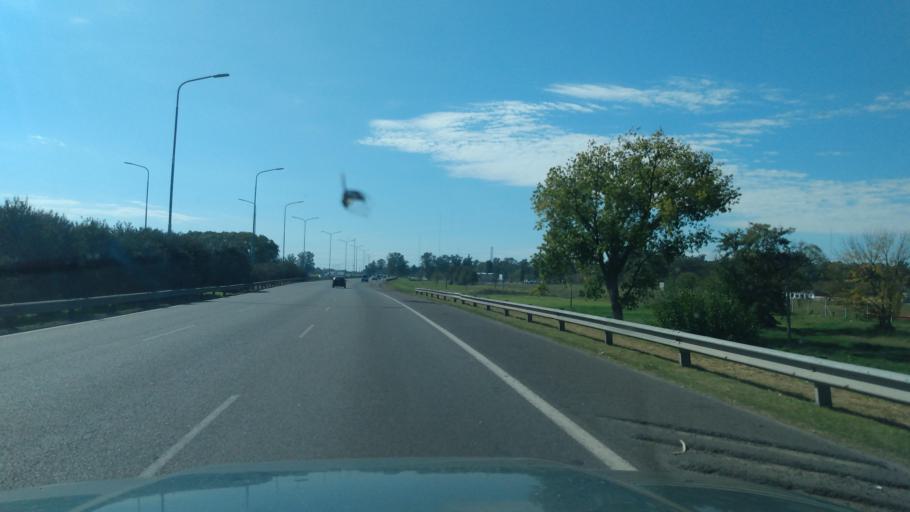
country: AR
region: Buenos Aires
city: Hurlingham
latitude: -34.5927
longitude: -58.6882
